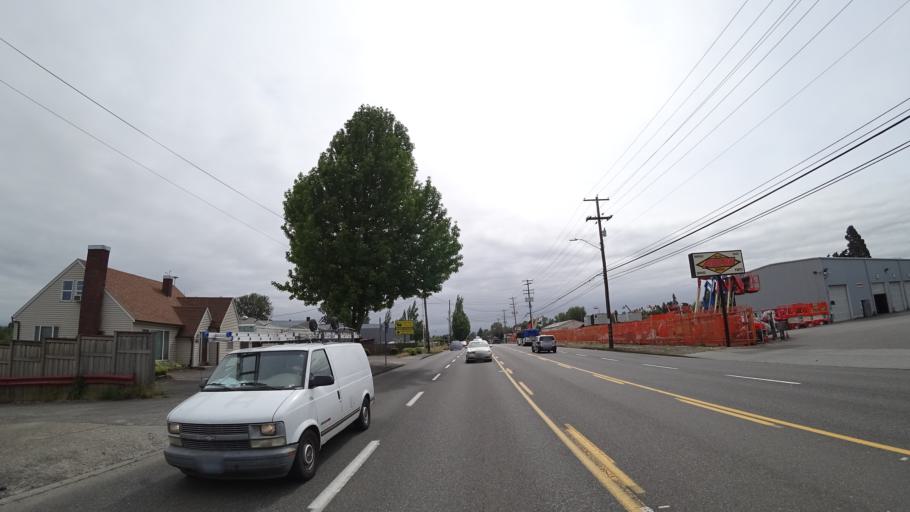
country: US
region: Oregon
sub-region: Multnomah County
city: Portland
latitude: 45.5725
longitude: -122.6242
